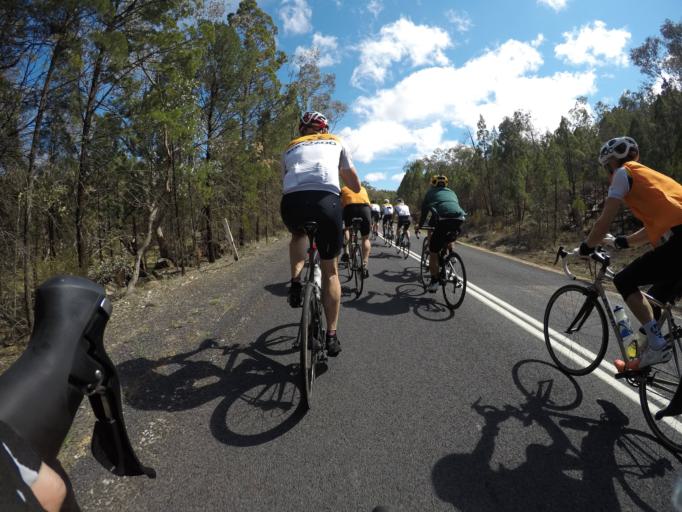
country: AU
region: New South Wales
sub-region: Parkes
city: Peak Hill
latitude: -32.6552
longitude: 148.5495
